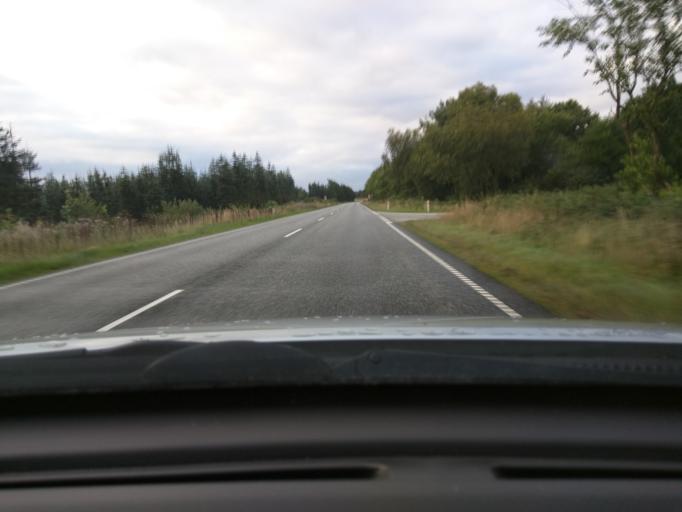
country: DK
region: Central Jutland
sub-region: Ikast-Brande Kommune
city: Bording Kirkeby
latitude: 56.2562
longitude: 9.3180
